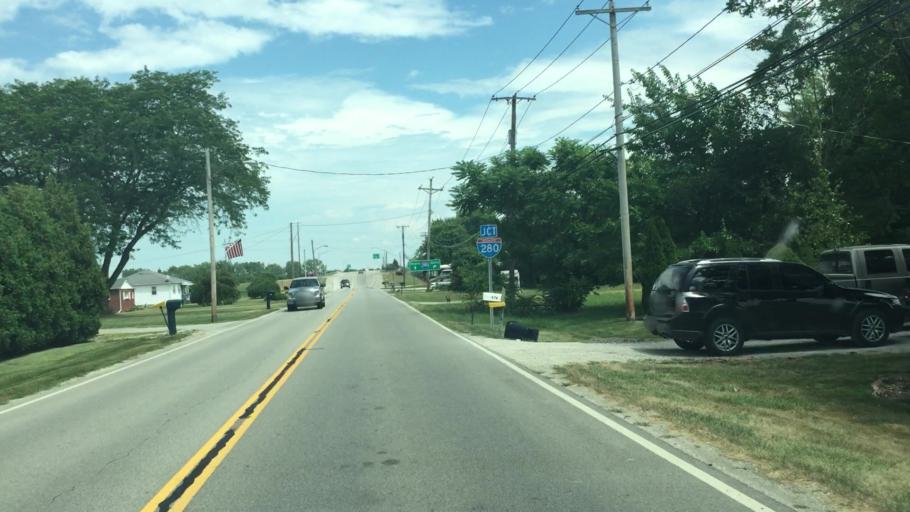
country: US
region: Ohio
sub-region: Wood County
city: Walbridge
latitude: 41.5879
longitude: -83.4829
